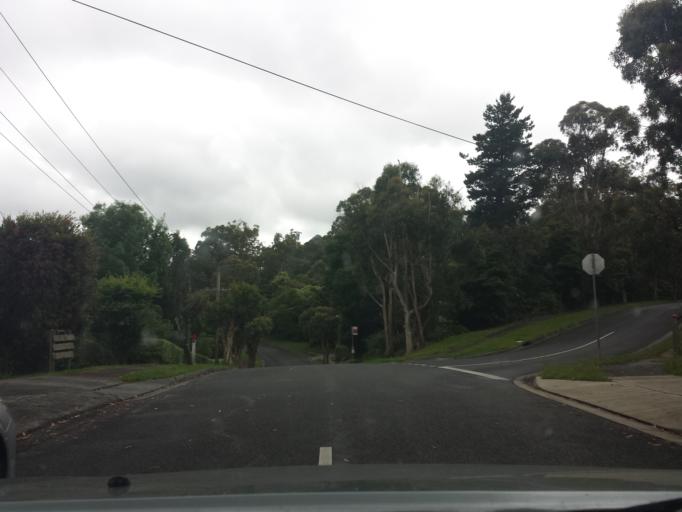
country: AU
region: Victoria
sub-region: Yarra Ranges
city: Belgrave Heights
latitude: -37.9143
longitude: 145.3451
